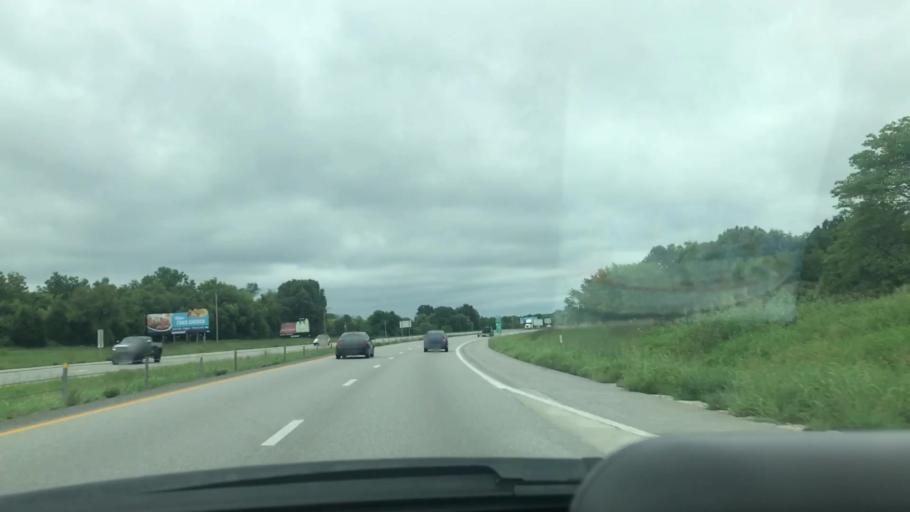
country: US
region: Missouri
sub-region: Greene County
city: Springfield
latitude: 37.2492
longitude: -93.3423
